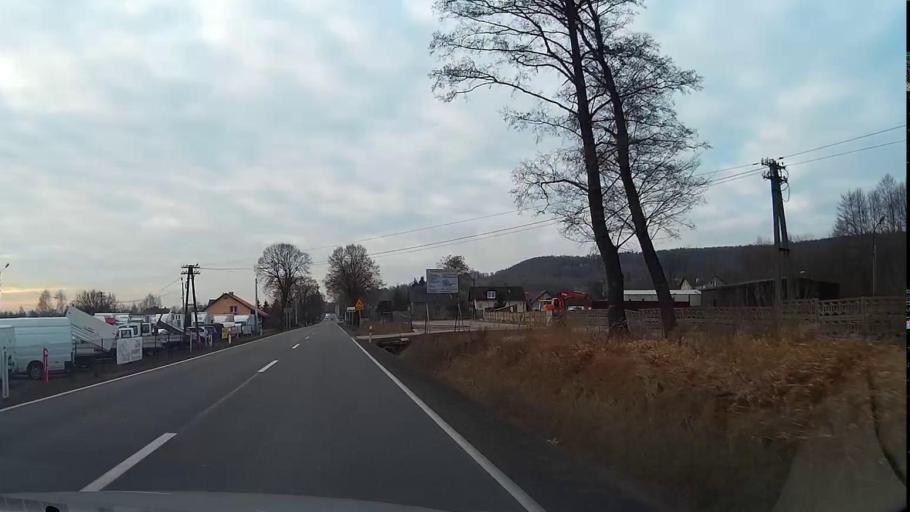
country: PL
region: Lesser Poland Voivodeship
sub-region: Powiat chrzanowski
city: Babice
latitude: 50.0689
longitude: 19.4657
